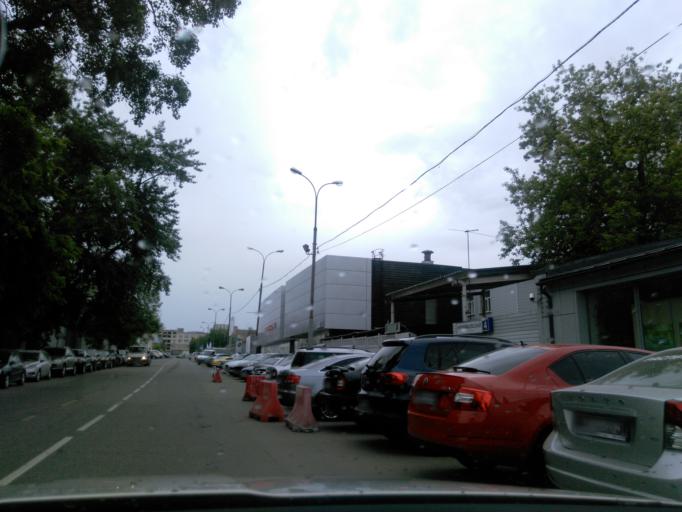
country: RU
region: Moscow
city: Taganskiy
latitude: 55.7328
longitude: 37.6854
